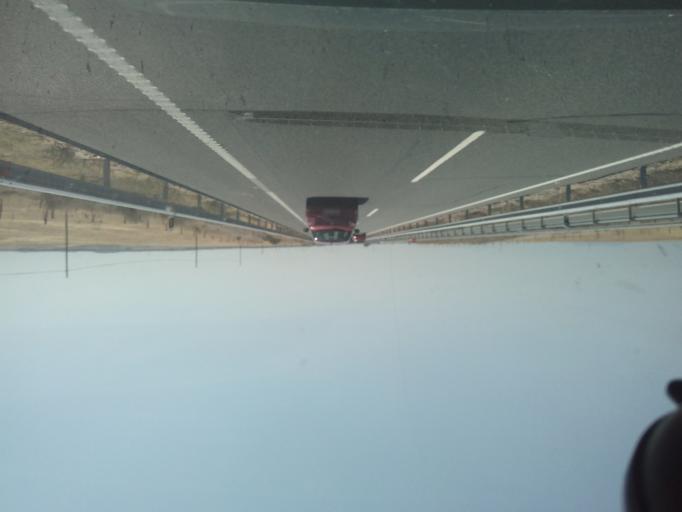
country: ES
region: Extremadura
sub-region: Provincia de Caceres
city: Berrocalejo
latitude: 39.8925
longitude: -5.3767
